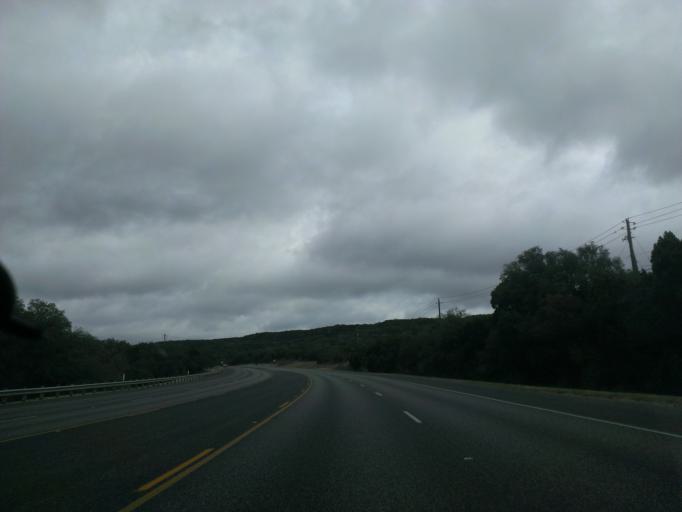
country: US
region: Texas
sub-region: Williamson County
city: Jollyville
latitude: 30.3784
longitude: -97.8060
